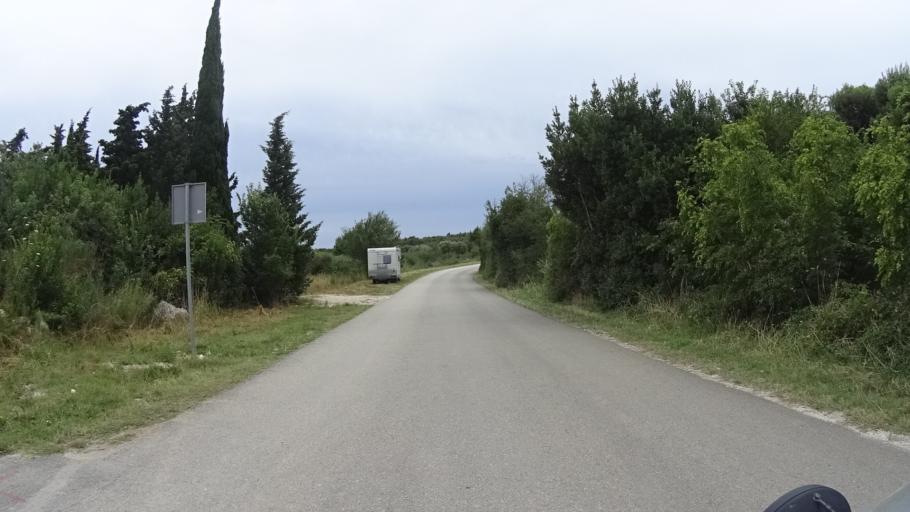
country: HR
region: Istarska
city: Medulin
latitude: 44.8016
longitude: 13.9062
